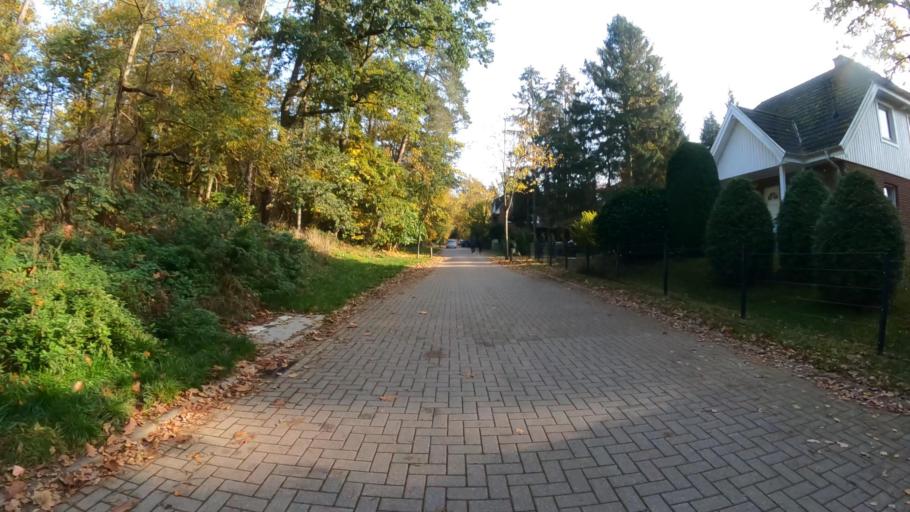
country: DE
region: Lower Saxony
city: Buchholz in der Nordheide
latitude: 53.3289
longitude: 9.8646
